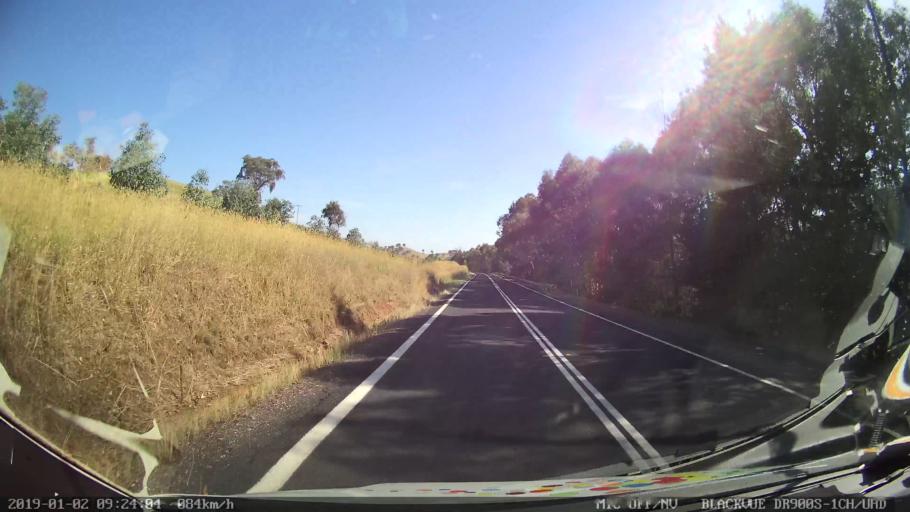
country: AU
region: New South Wales
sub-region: Tumut Shire
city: Tumut
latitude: -35.3818
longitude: 148.2915
